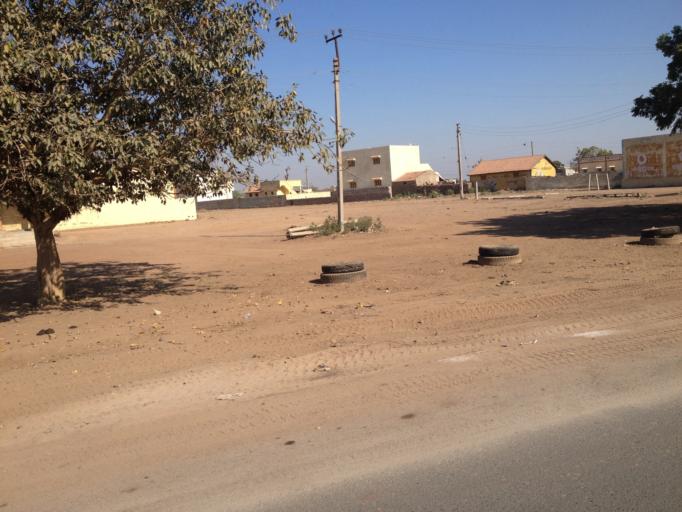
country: IN
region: Gujarat
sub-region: Kachchh
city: Anjar
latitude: 23.1852
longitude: 69.9074
